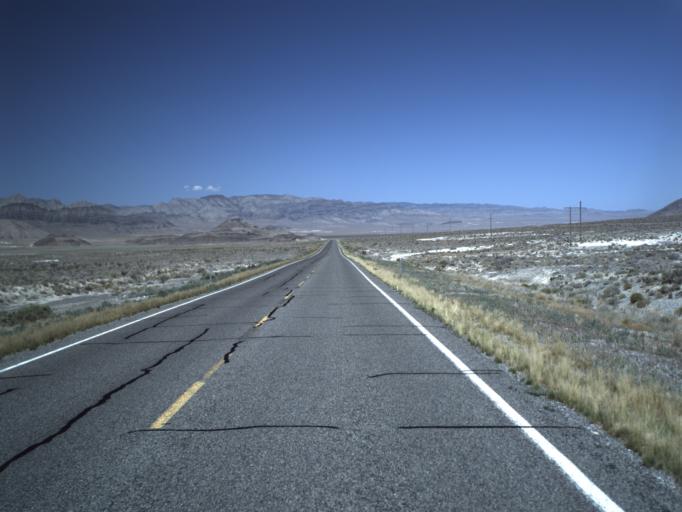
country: US
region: Utah
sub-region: Beaver County
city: Milford
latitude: 39.0349
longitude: -113.3900
